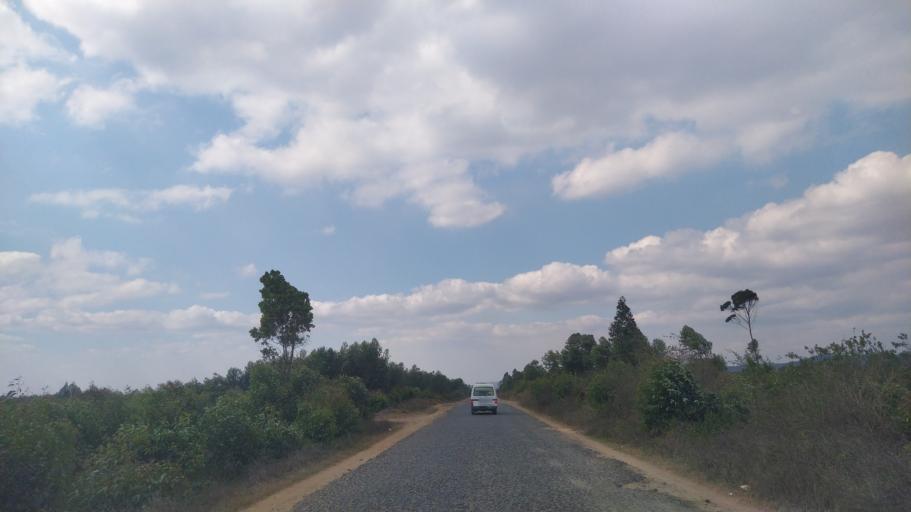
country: MG
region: Alaotra Mangoro
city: Moramanga
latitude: -18.7716
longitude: 48.2509
